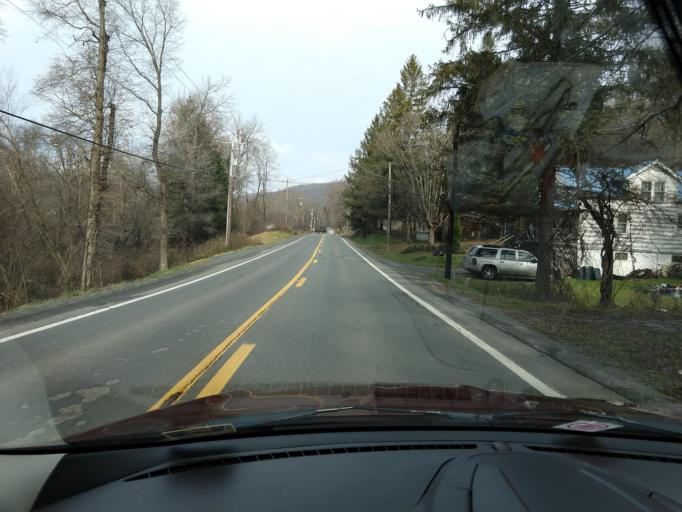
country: US
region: West Virginia
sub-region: Greenbrier County
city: Rainelle
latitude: 37.9757
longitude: -80.7098
